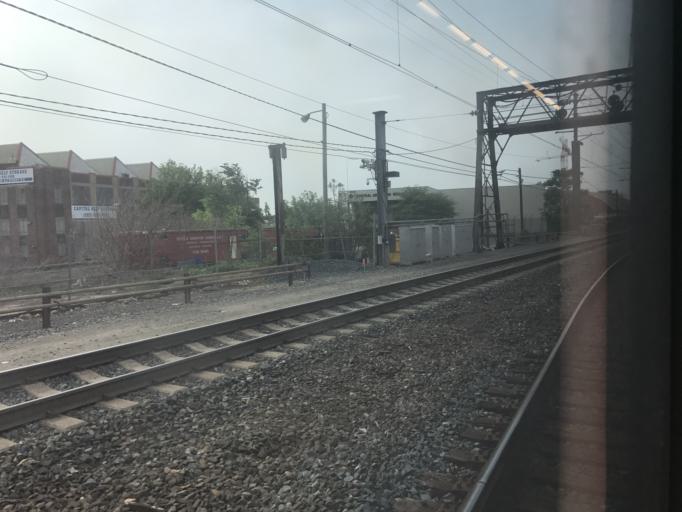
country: US
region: Washington, D.C.
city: Washington, D.C.
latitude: 38.9079
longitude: -77.0026
